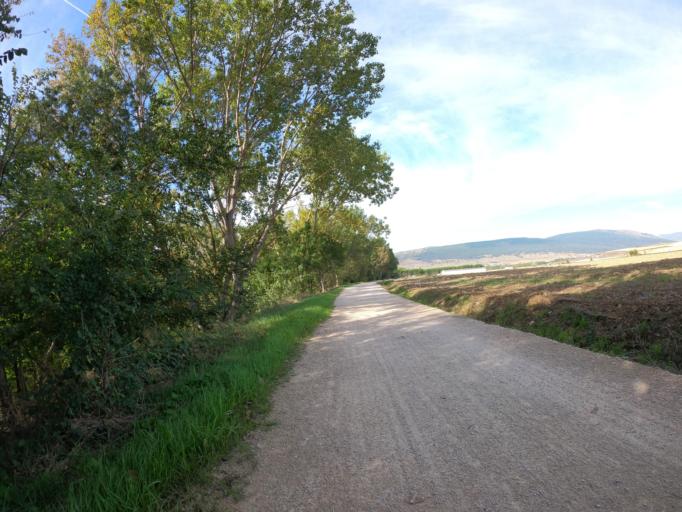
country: ES
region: Navarre
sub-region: Provincia de Navarra
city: Oltza
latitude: 42.8121
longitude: -1.7530
